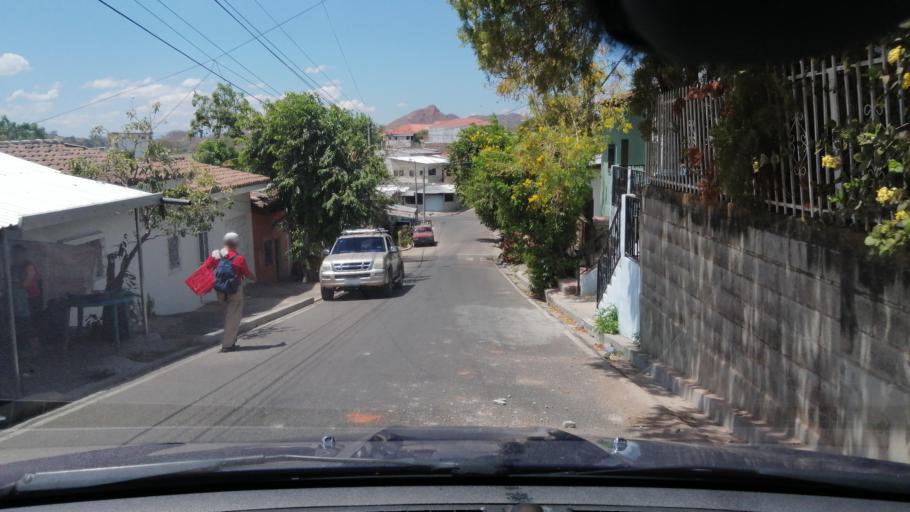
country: SV
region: Santa Ana
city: Metapan
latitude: 14.3328
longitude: -89.4389
